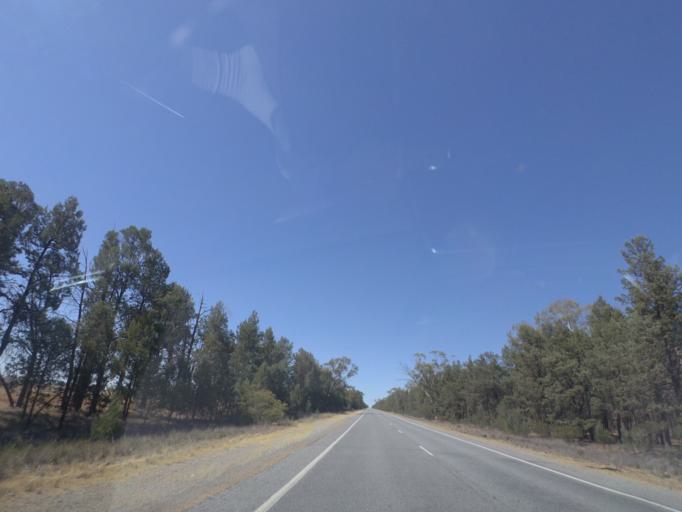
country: AU
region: New South Wales
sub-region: Narrandera
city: Narrandera
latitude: -34.4236
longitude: 146.8445
